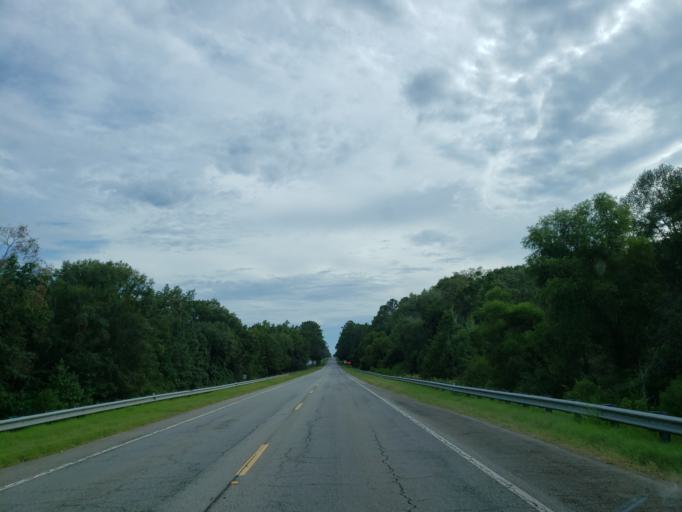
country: US
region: Georgia
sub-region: Tift County
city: Tifton
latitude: 31.5323
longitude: -83.3994
